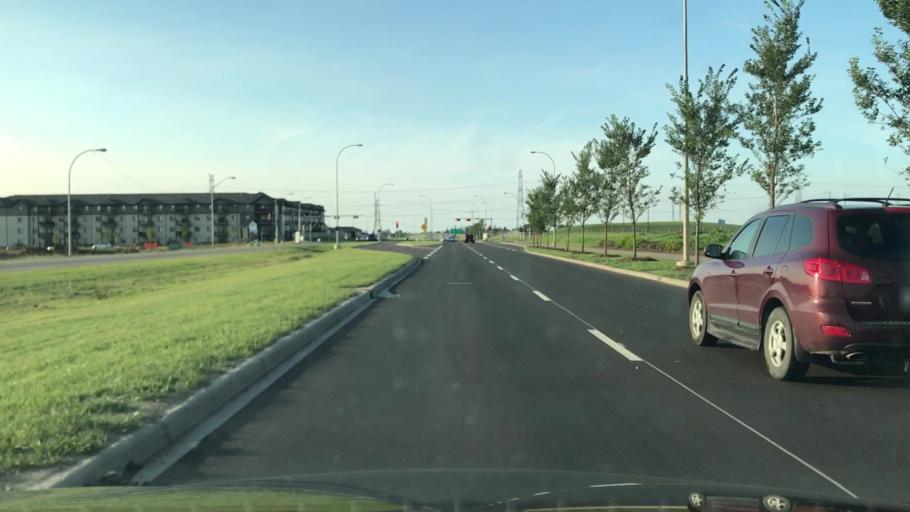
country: CA
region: Alberta
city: Beaumont
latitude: 53.4265
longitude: -113.4178
